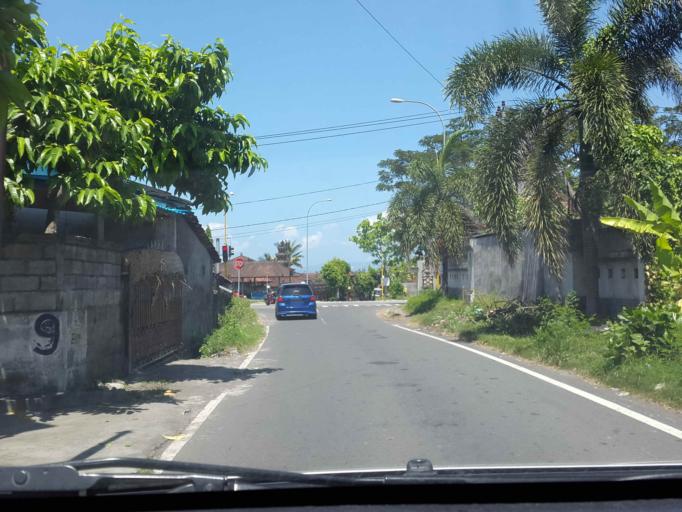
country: ID
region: Bali
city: Dawan
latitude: -8.5612
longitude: 115.4202
